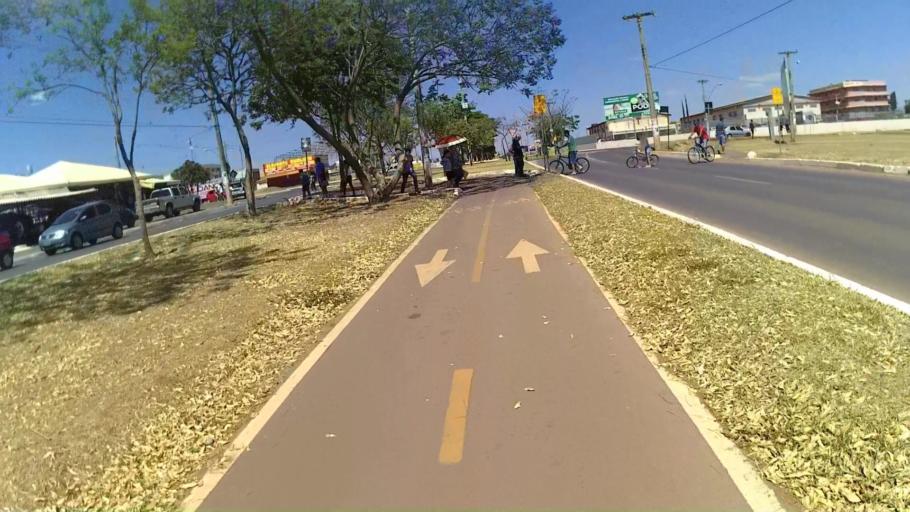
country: BR
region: Federal District
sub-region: Brasilia
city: Brasilia
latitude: -15.8975
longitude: -48.0437
